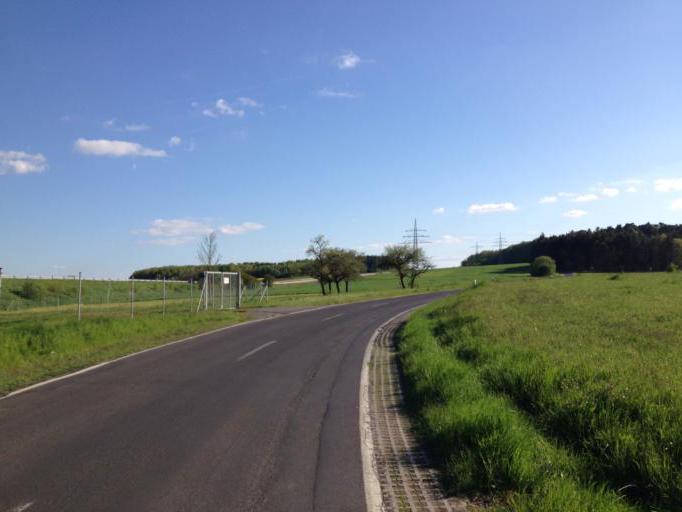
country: DE
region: Hesse
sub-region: Regierungsbezirk Giessen
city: Grossen Buseck
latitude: 50.5770
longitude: 8.8018
